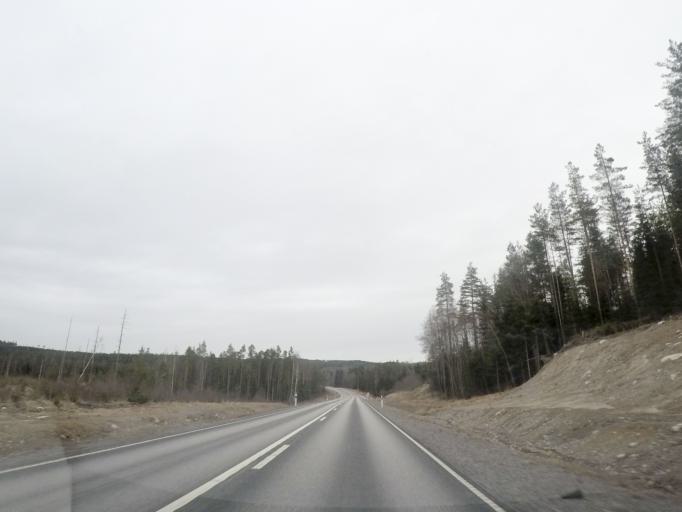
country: SE
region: Dalarna
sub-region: Ludvika Kommun
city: Grangesberg
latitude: 59.9814
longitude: 15.0205
